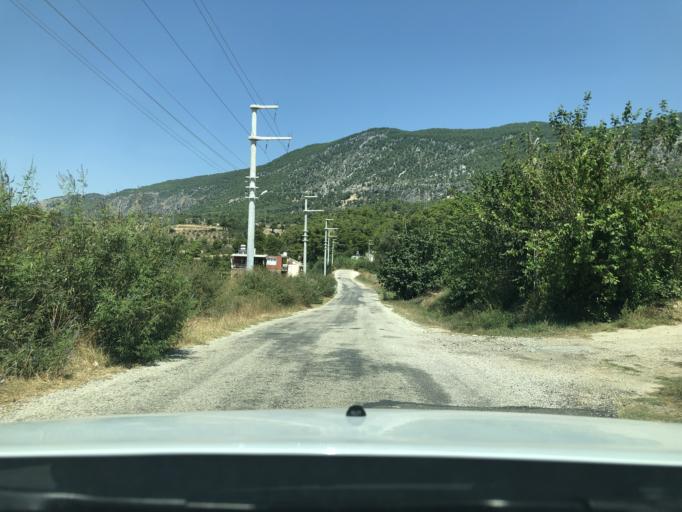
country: TR
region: Antalya
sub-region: Manavgat
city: Kizilagac
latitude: 36.8584
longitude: 31.5632
